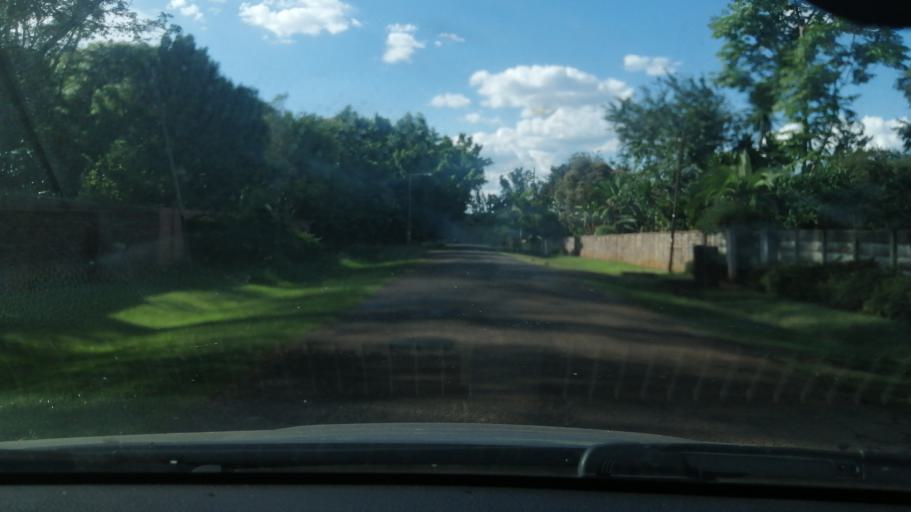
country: ZW
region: Harare
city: Harare
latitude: -17.7668
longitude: 31.0613
